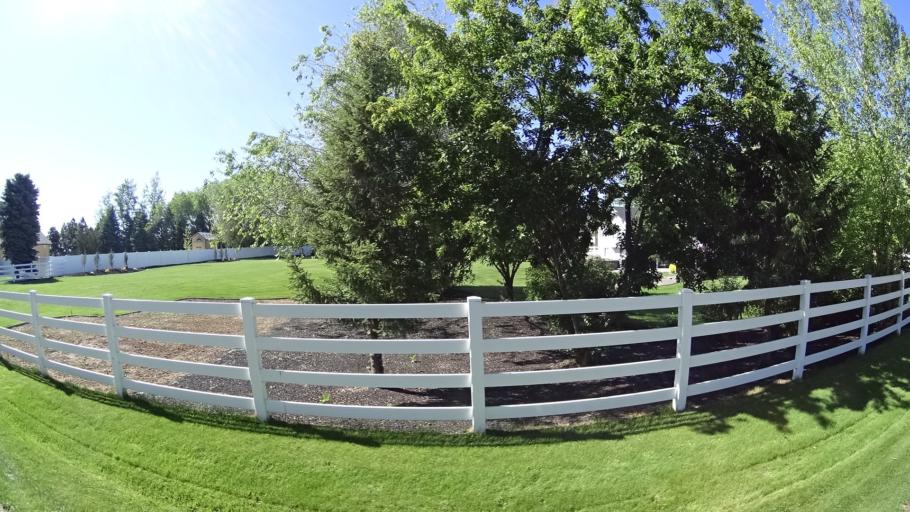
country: US
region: Idaho
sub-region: Ada County
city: Meridian
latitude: 43.6653
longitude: -116.4016
